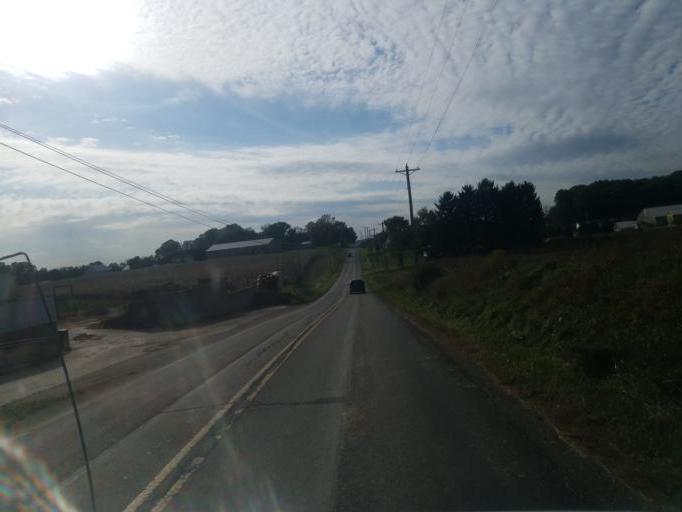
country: US
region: Ohio
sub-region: Wayne County
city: Apple Creek
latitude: 40.6894
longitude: -81.8386
